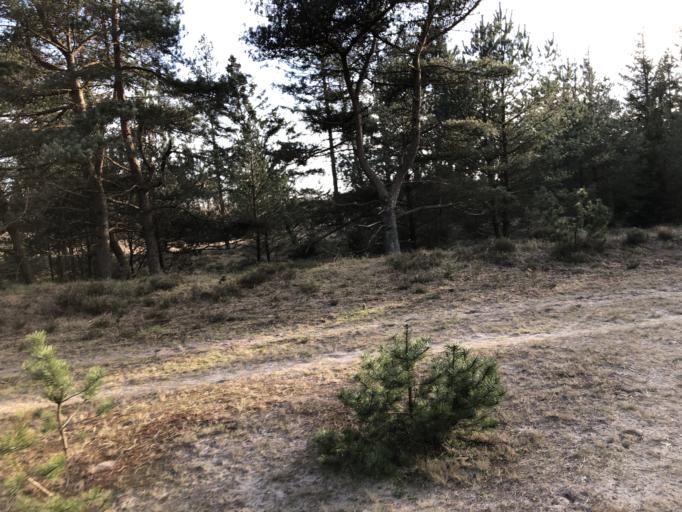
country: DK
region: Central Jutland
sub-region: Holstebro Kommune
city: Ulfborg
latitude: 56.2473
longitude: 8.4437
